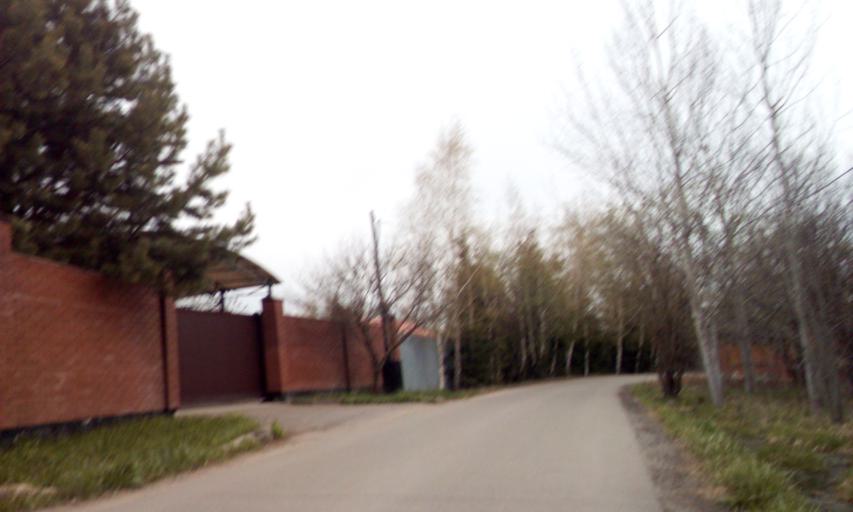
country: RU
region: Moskovskaya
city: Gorki Vtoryye
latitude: 55.6755
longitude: 37.1470
